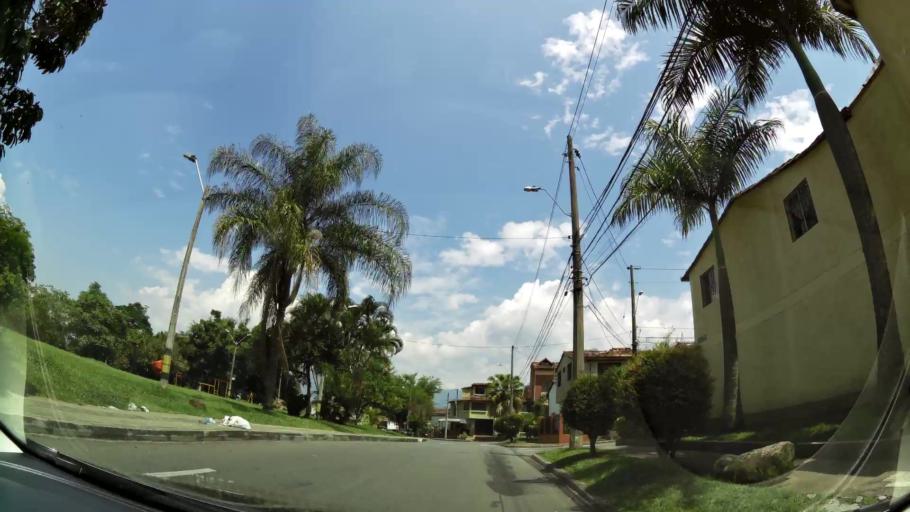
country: CO
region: Antioquia
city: Itagui
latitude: 6.2212
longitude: -75.6085
